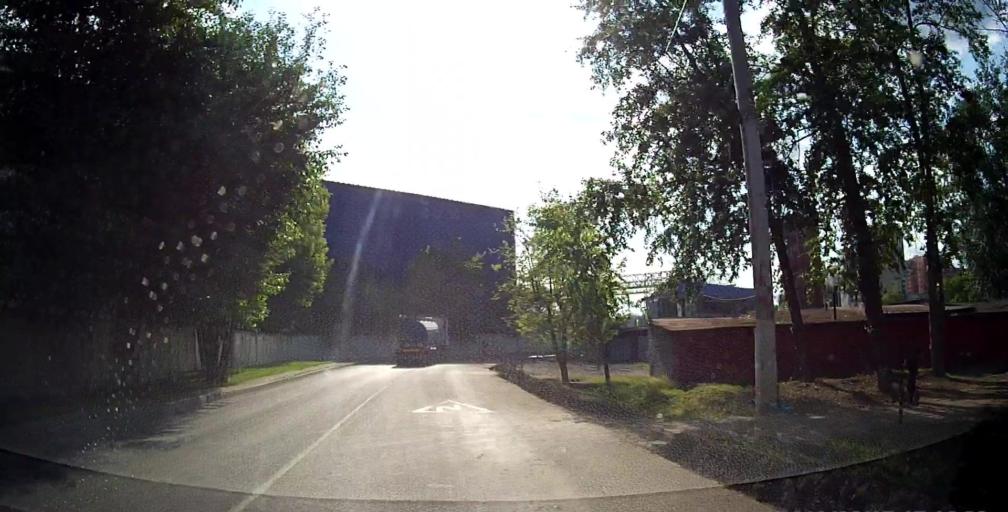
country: RU
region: Moskovskaya
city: Shcherbinka
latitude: 55.4997
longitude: 37.5645
